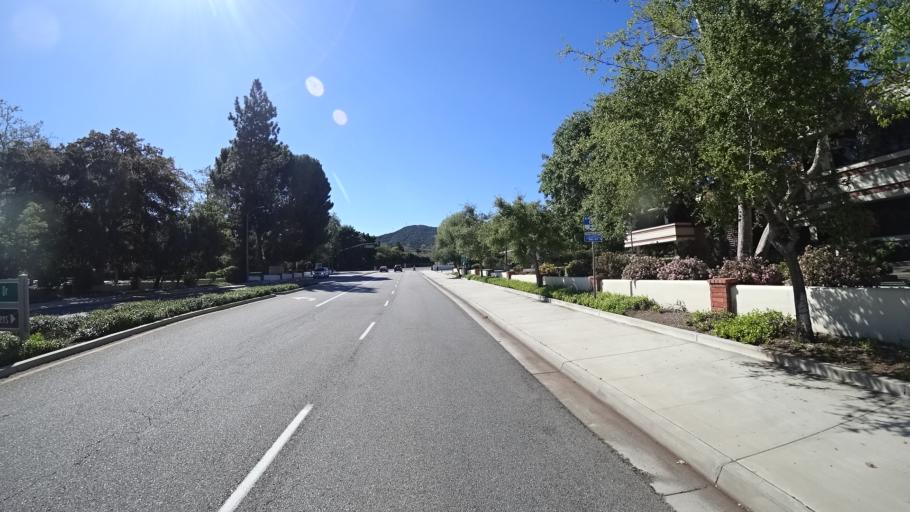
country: US
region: California
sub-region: Ventura County
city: Thousand Oaks
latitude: 34.1762
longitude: -118.8766
